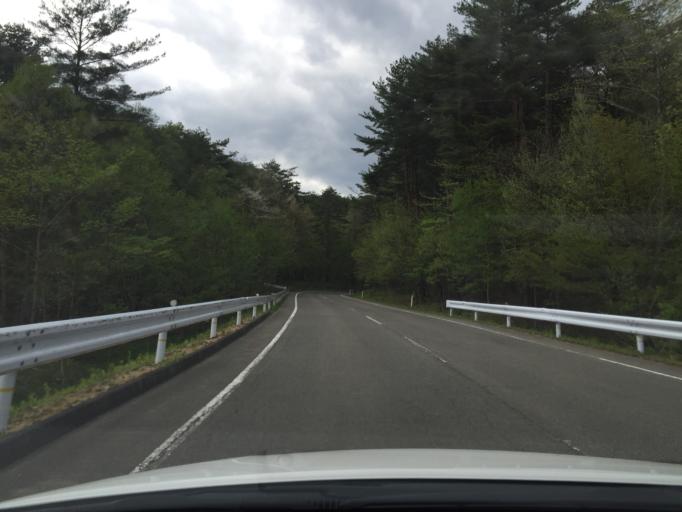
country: JP
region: Miyagi
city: Marumori
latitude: 37.6890
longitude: 140.7964
